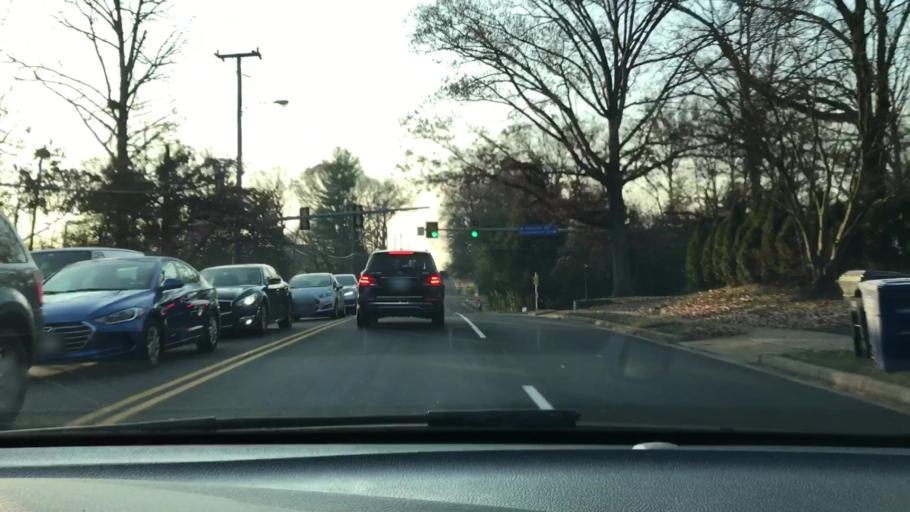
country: US
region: Virginia
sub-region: Fairfax County
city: Annandale
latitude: 38.8422
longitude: -77.2000
